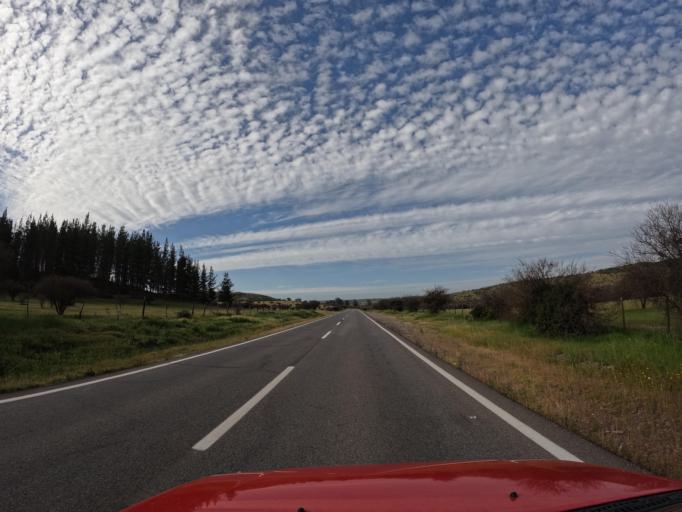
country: CL
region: O'Higgins
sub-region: Provincia de Colchagua
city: Santa Cruz
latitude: -34.3002
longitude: -71.7337
